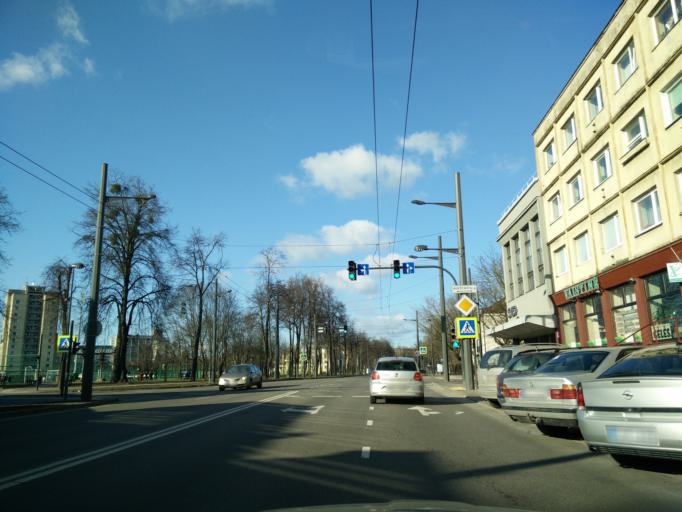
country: LT
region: Kauno apskritis
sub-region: Kaunas
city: Eiguliai
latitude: 54.9026
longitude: 23.9314
